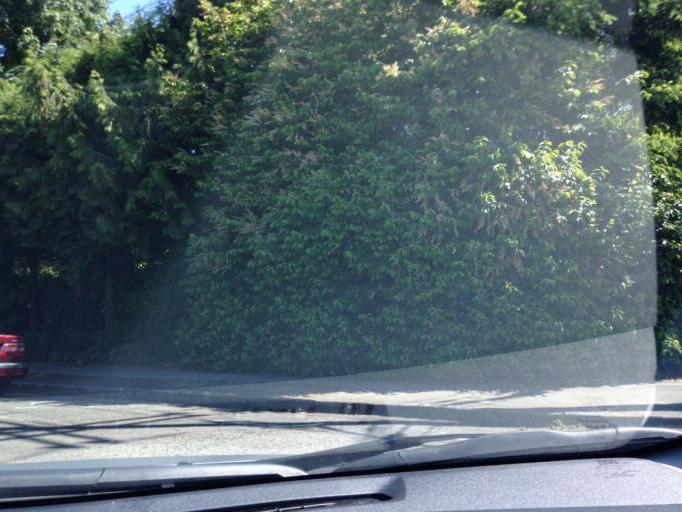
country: US
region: Washington
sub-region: King County
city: Mercer Island
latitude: 47.5496
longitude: -122.2588
